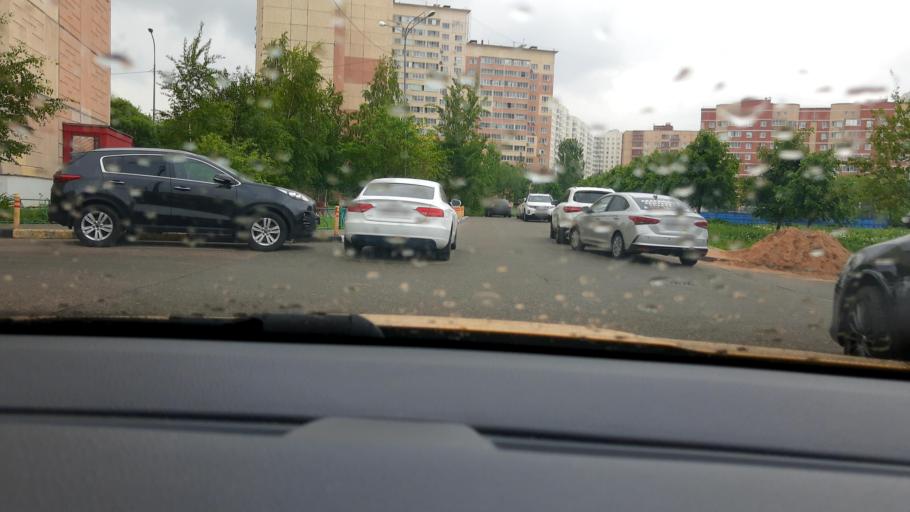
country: RU
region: Moscow
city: Vatutino
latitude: 55.9053
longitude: 37.7009
